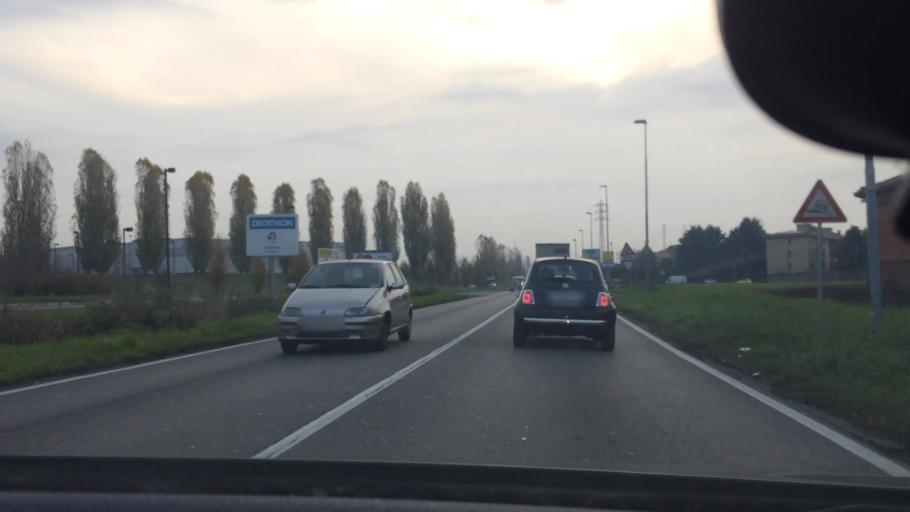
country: IT
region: Lombardy
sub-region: Provincia di Monza e Brianza
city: Varedo
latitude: 45.6028
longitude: 9.1619
